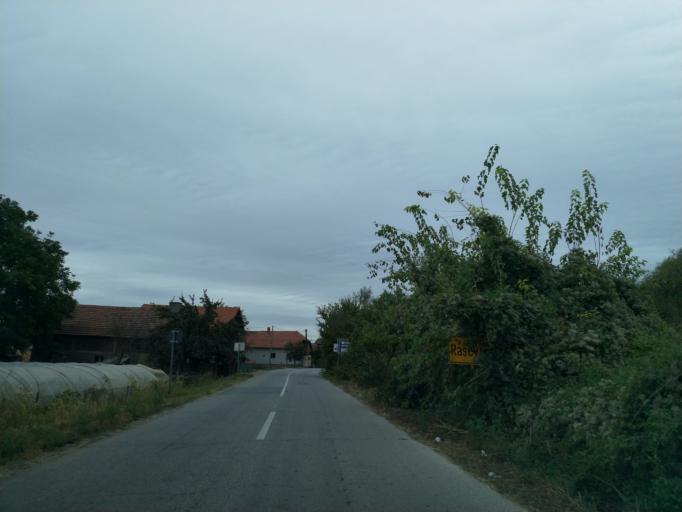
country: RS
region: Central Serbia
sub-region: Pomoravski Okrug
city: Paracin
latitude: 43.8439
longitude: 21.3225
